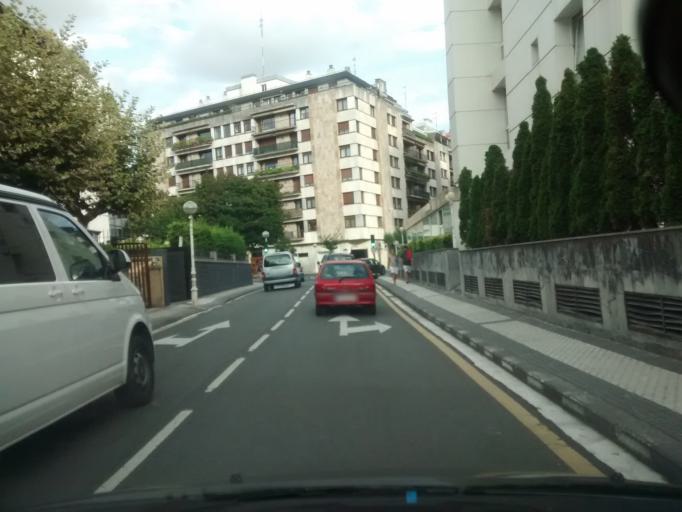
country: ES
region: Basque Country
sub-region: Provincia de Guipuzcoa
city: San Sebastian
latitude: 43.3143
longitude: -2.0044
